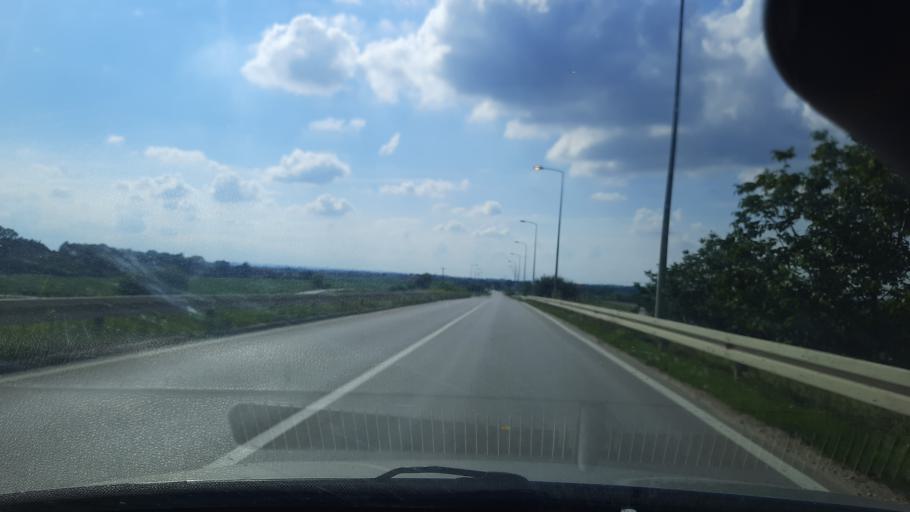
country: RS
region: Central Serbia
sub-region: Branicevski Okrug
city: Pozarevac
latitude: 44.5982
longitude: 21.1526
